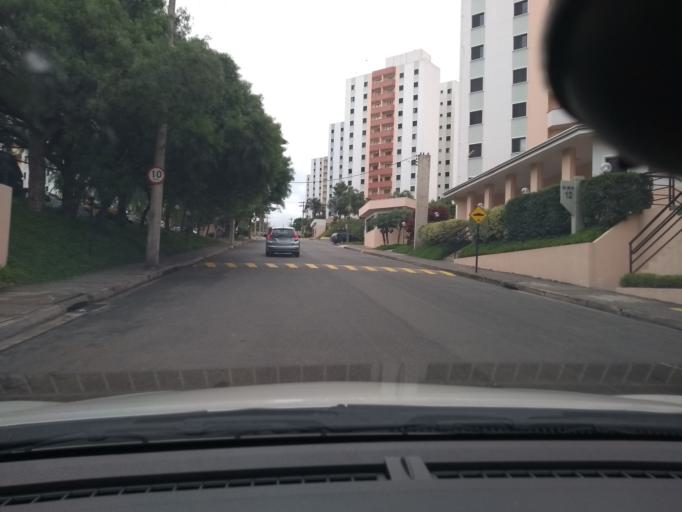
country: BR
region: Sao Paulo
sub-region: Jundiai
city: Jundiai
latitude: -23.1884
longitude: -46.9567
